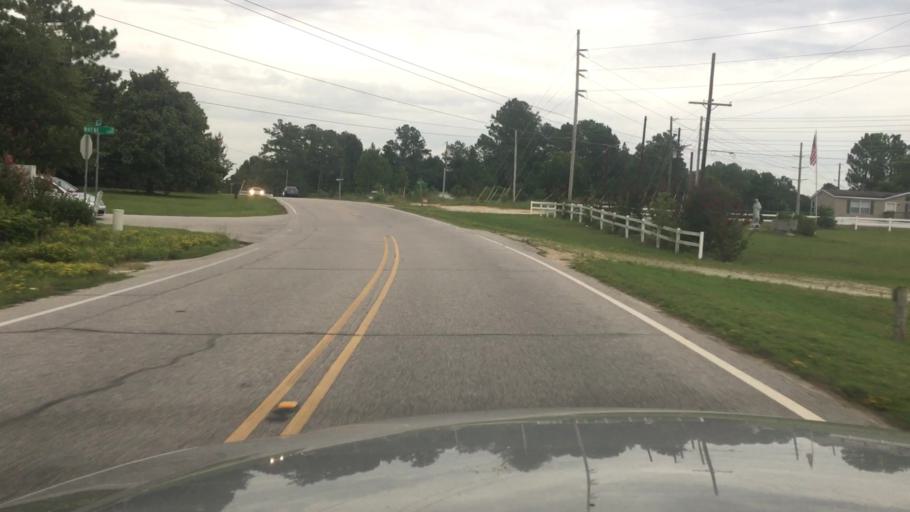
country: US
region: North Carolina
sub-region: Hoke County
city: Rockfish
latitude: 34.9815
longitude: -79.0344
